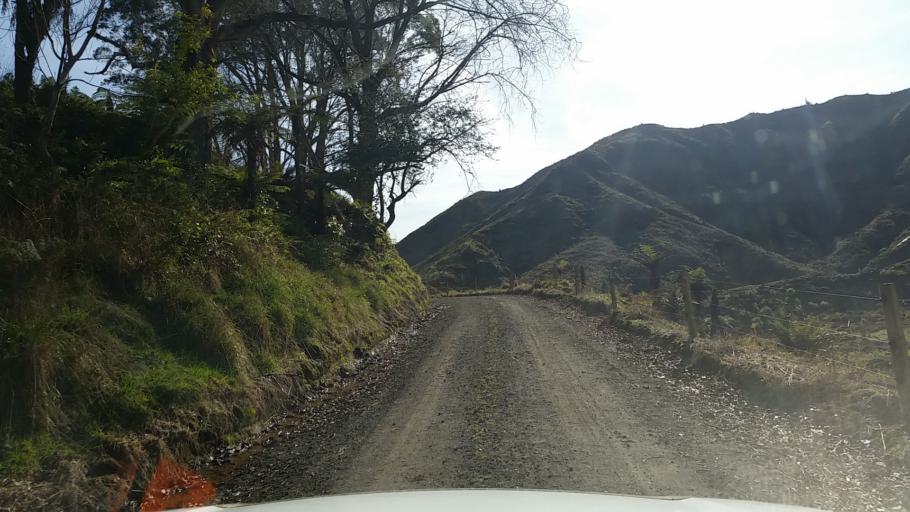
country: NZ
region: Taranaki
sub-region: South Taranaki District
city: Eltham
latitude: -39.3625
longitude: 174.5151
